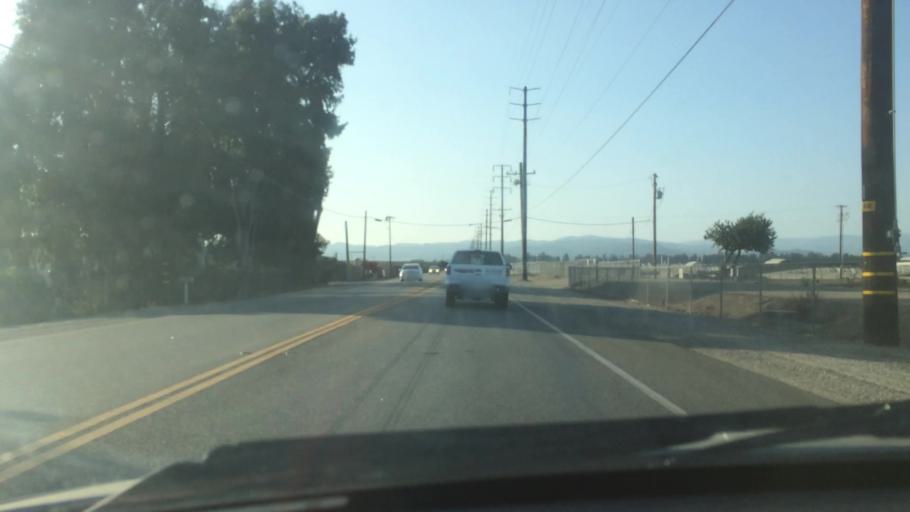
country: US
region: California
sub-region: Ventura County
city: Saticoy
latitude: 34.2591
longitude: -119.1136
